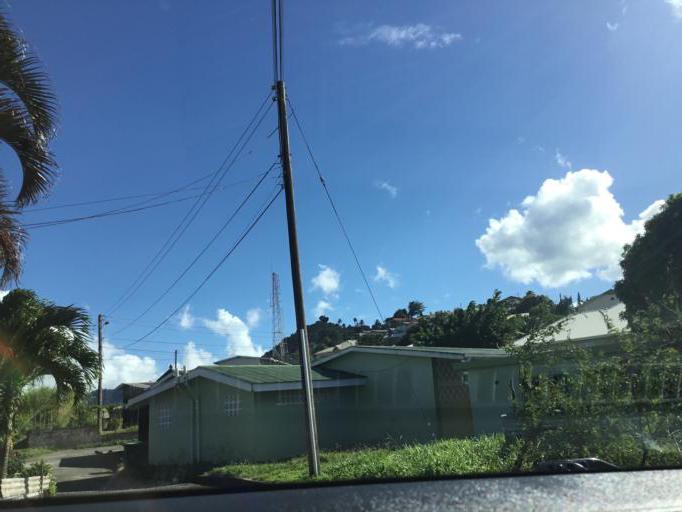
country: VC
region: Saint David
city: Chateaubelair
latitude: 13.2716
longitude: -61.2389
